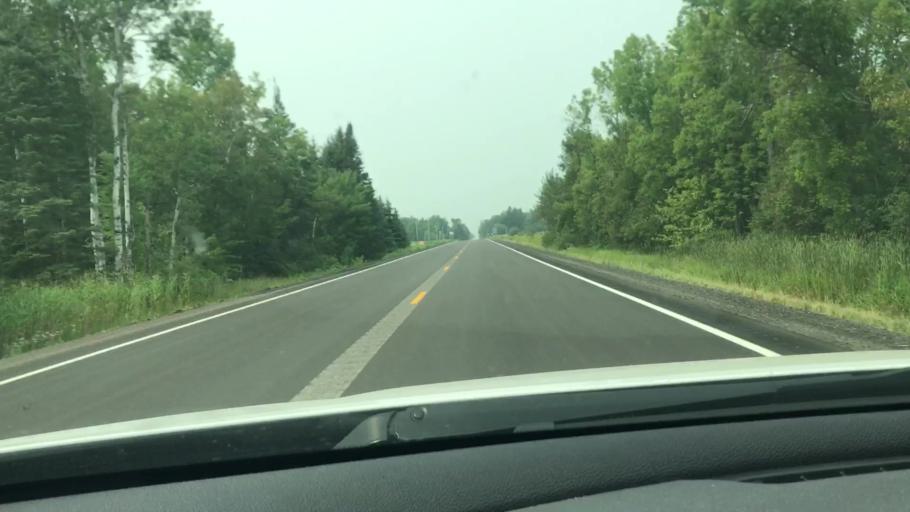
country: US
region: Minnesota
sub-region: Itasca County
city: Cohasset
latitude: 47.3537
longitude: -93.8459
